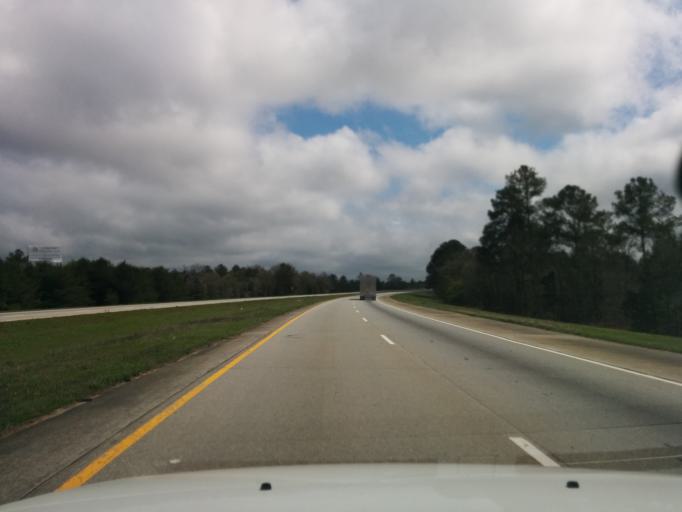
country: US
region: Georgia
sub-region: Emanuel County
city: Swainsboro
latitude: 32.4081
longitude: -82.3217
